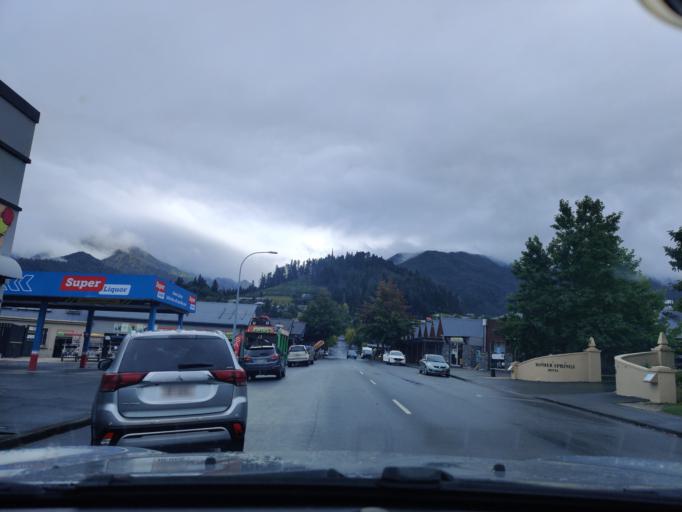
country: NZ
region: Canterbury
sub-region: Hurunui District
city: Amberley
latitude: -42.5209
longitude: 172.8295
